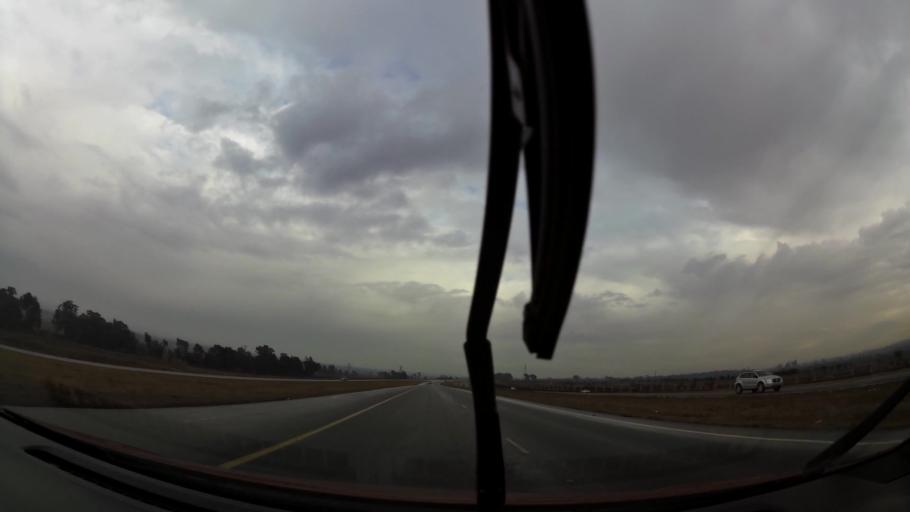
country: ZA
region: Gauteng
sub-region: City of Johannesburg Metropolitan Municipality
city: Soweto
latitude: -26.3045
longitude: 27.8704
